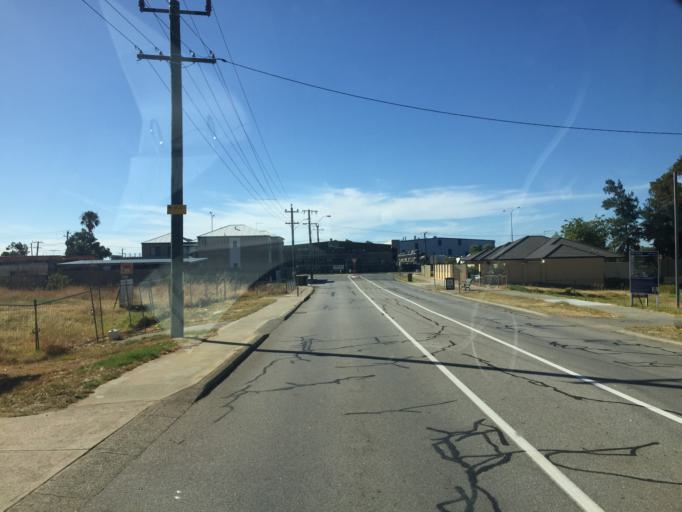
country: AU
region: Western Australia
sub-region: Gosnells
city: Maddington
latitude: -32.0455
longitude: 115.9908
